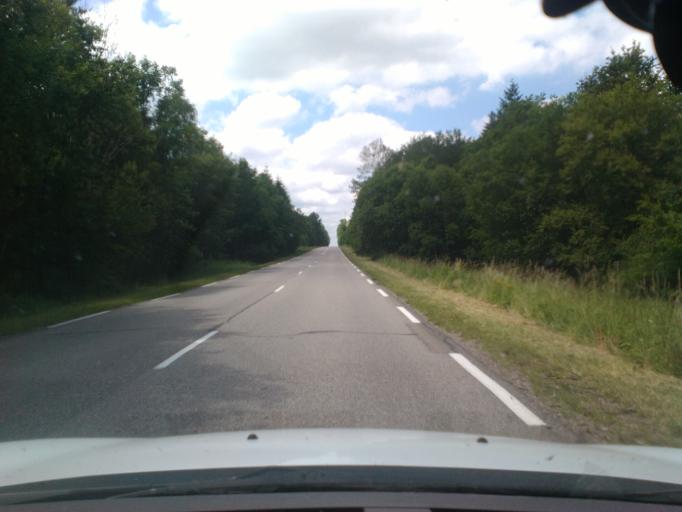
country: FR
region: Lorraine
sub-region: Departement des Vosges
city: Aydoilles
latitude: 48.2074
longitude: 6.5495
